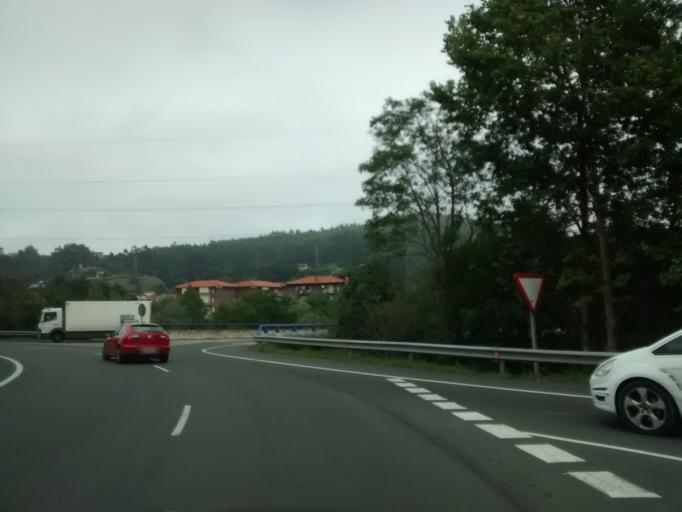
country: ES
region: Cantabria
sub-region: Provincia de Cantabria
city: Torrelavega
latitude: 43.3563
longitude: -4.0648
